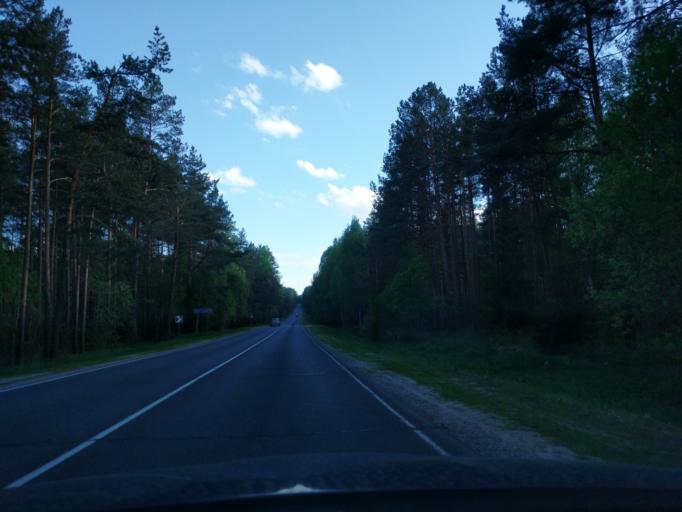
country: BY
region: Minsk
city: Kryvichy
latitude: 54.7282
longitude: 27.1397
